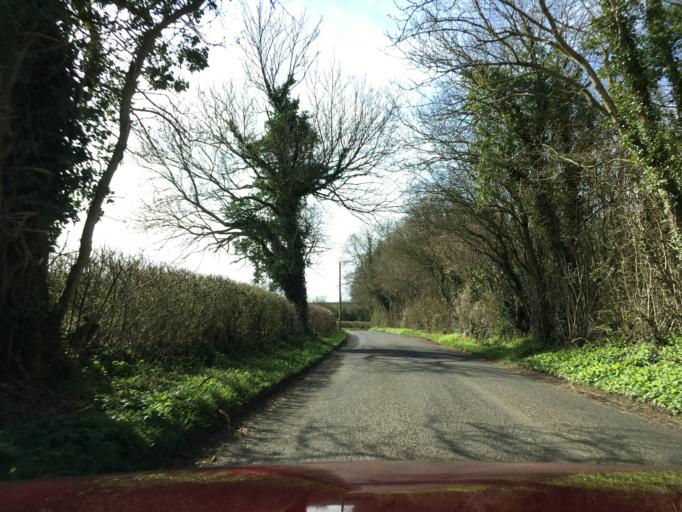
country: GB
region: England
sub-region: Wiltshire
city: Norton
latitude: 51.5222
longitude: -2.1622
